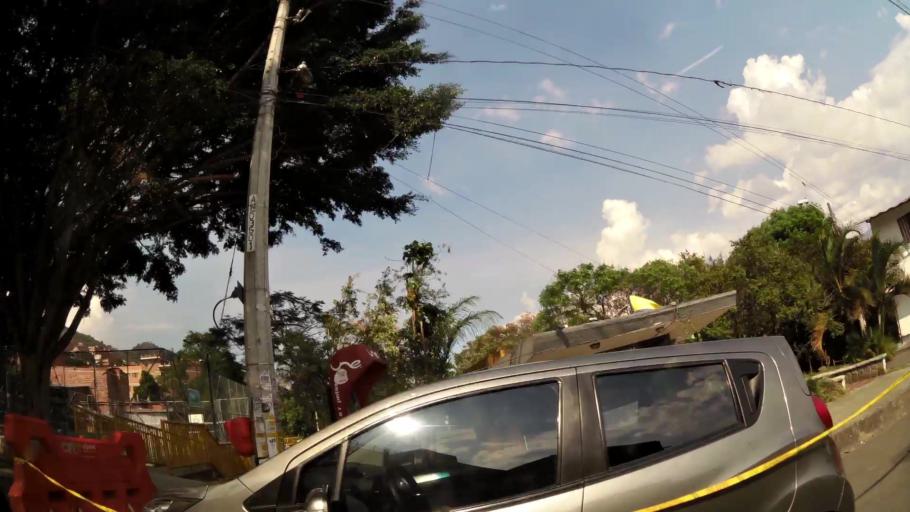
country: CO
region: Antioquia
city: Medellin
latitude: 6.2911
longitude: -75.5926
